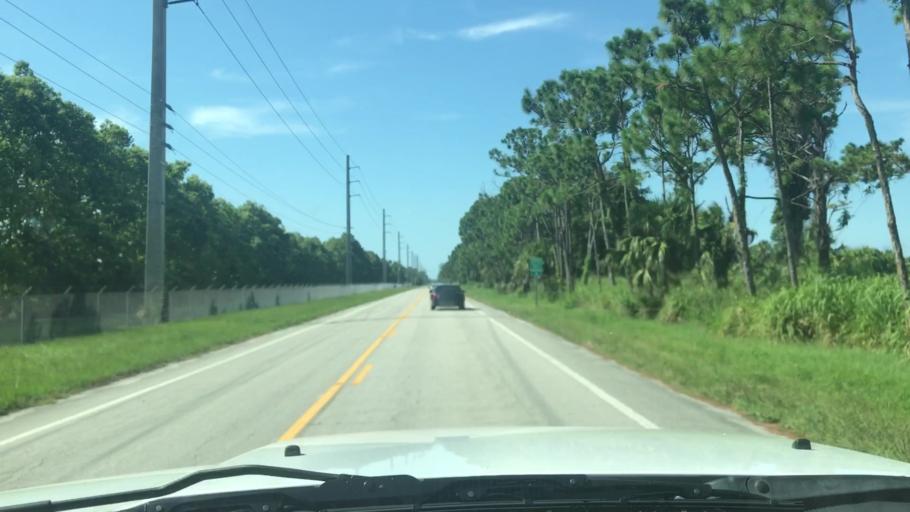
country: US
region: Florida
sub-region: Indian River County
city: Winter Beach
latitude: 27.7202
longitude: -80.4459
